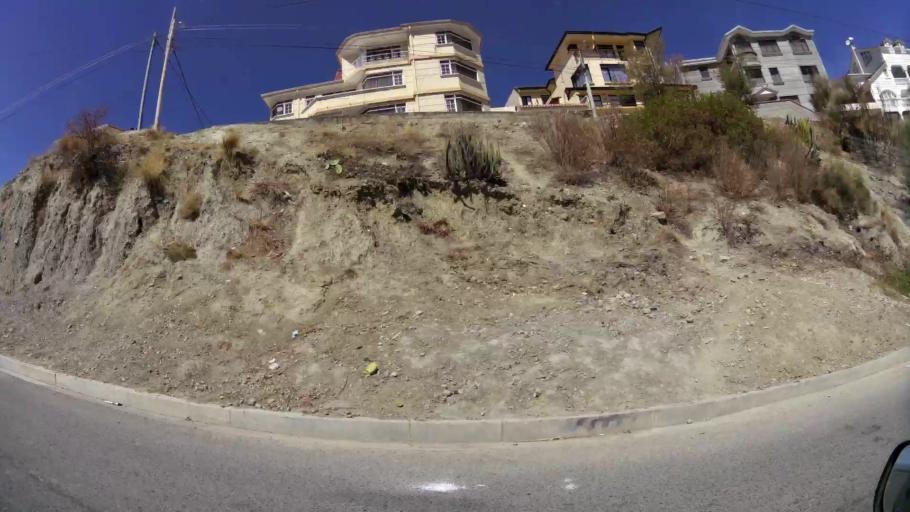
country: BO
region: La Paz
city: La Paz
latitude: -16.5363
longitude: -68.1016
